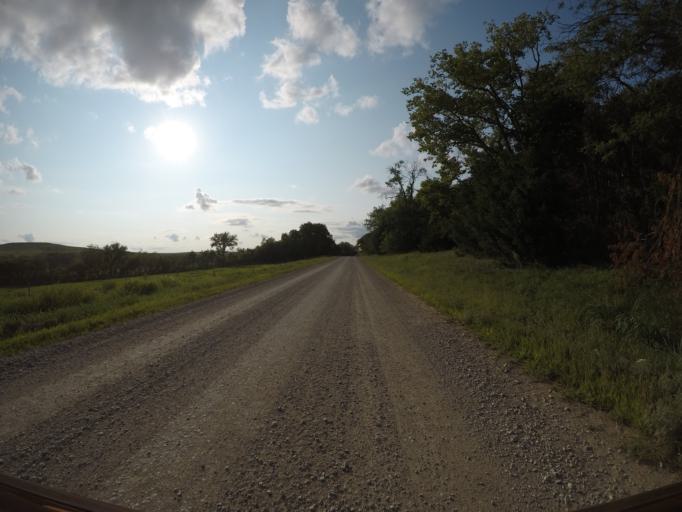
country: US
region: Kansas
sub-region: Wabaunsee County
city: Alma
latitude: 38.9152
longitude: -96.2143
